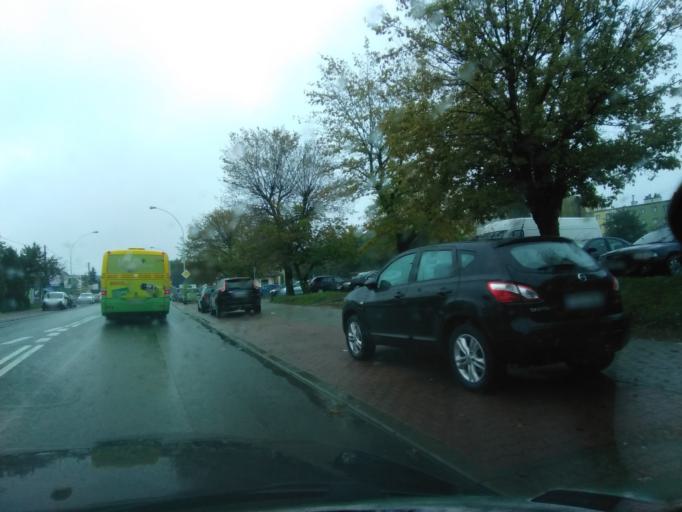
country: PL
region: Subcarpathian Voivodeship
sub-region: Powiat debicki
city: Debica
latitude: 50.0535
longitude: 21.4226
